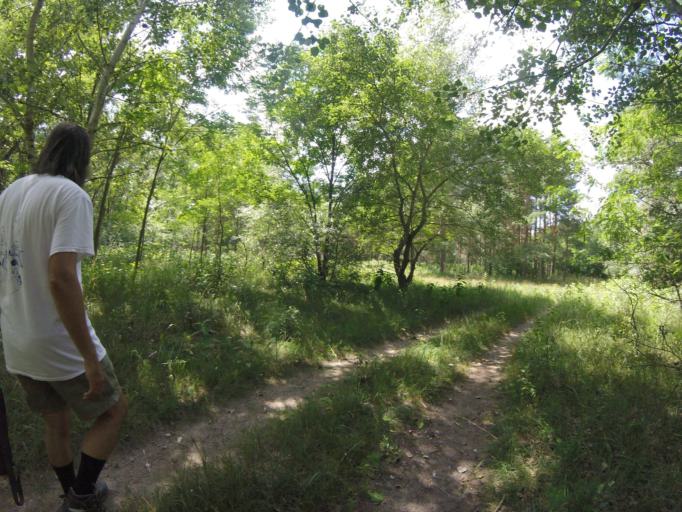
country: HU
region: Pest
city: Nagykoros
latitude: 47.0722
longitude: 19.7455
